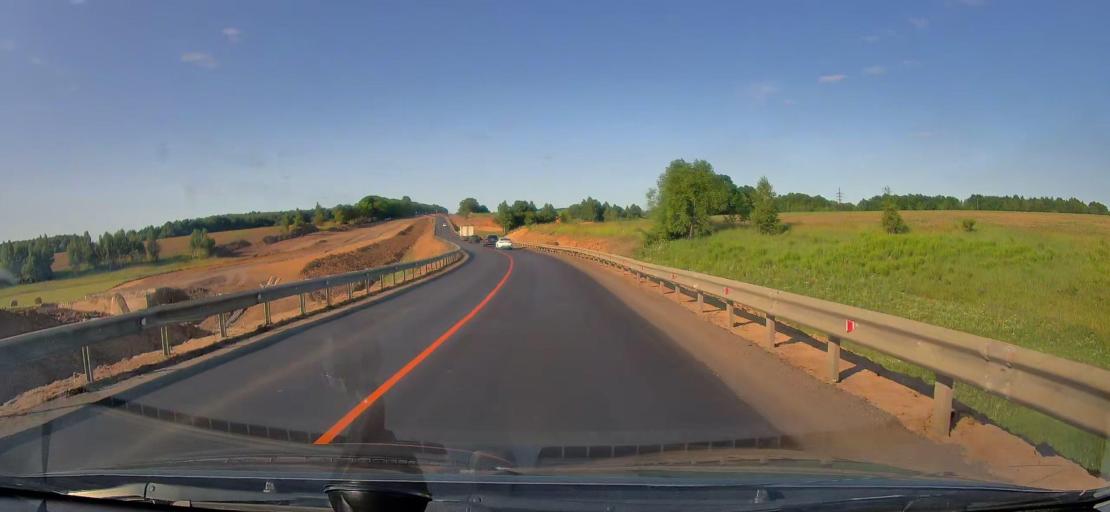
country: RU
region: Tula
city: Bol'shoye Skuratovo
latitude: 53.4158
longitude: 36.7804
